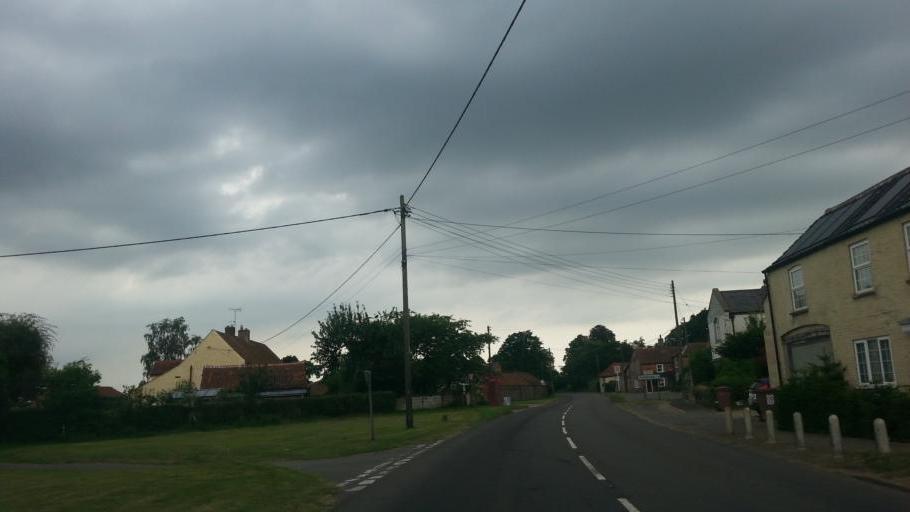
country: GB
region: England
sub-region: Norfolk
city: Fakenham
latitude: 52.8190
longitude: 0.6955
